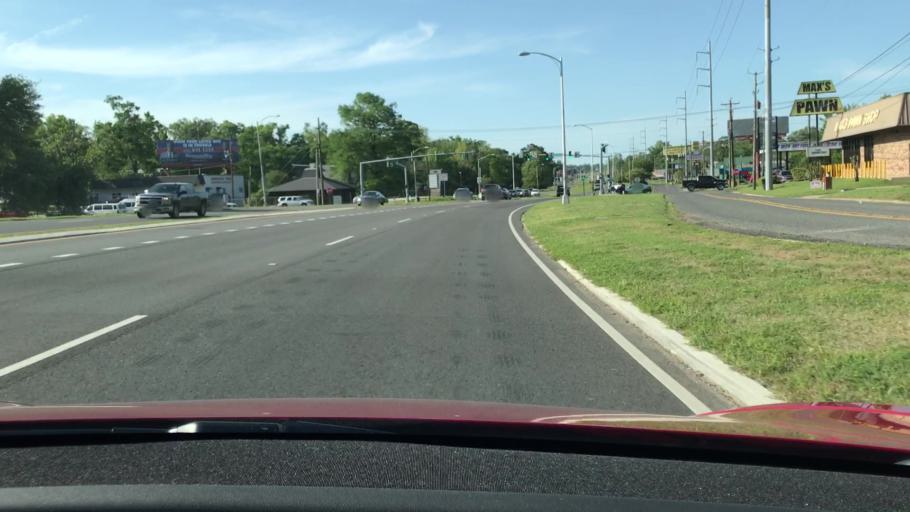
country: US
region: Louisiana
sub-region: Bossier Parish
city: Bossier City
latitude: 32.4838
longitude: -93.7239
